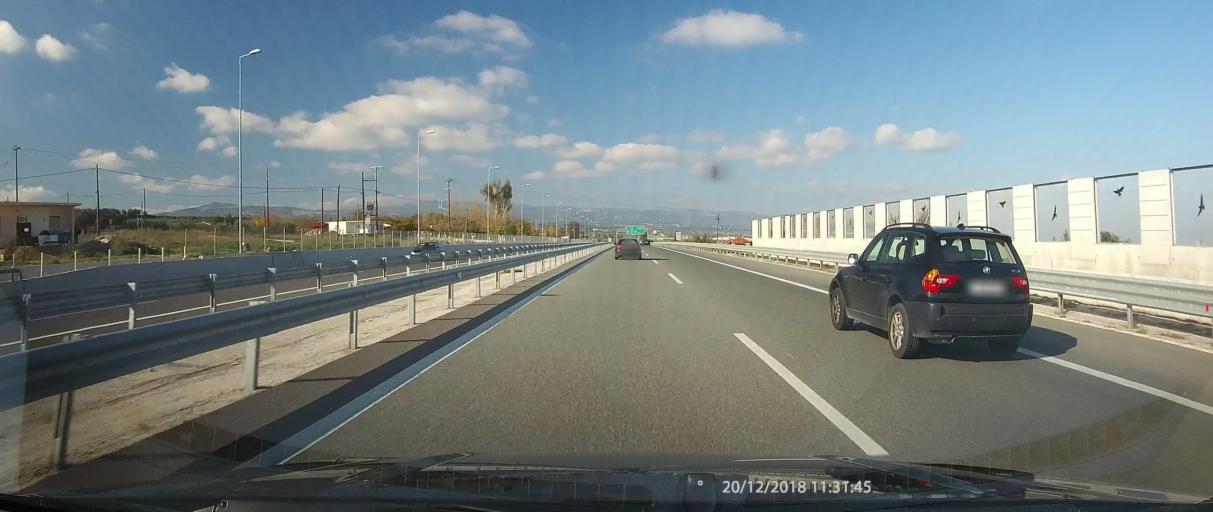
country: GR
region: Peloponnese
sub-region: Nomos Korinthias
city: Zevgolateio
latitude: 37.9244
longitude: 22.8041
